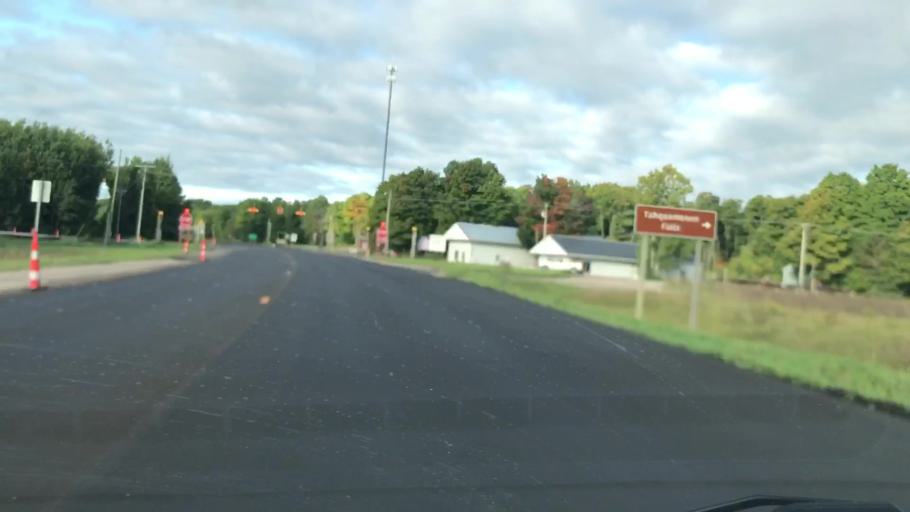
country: US
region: Michigan
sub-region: Luce County
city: Newberry
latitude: 46.3460
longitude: -85.0295
